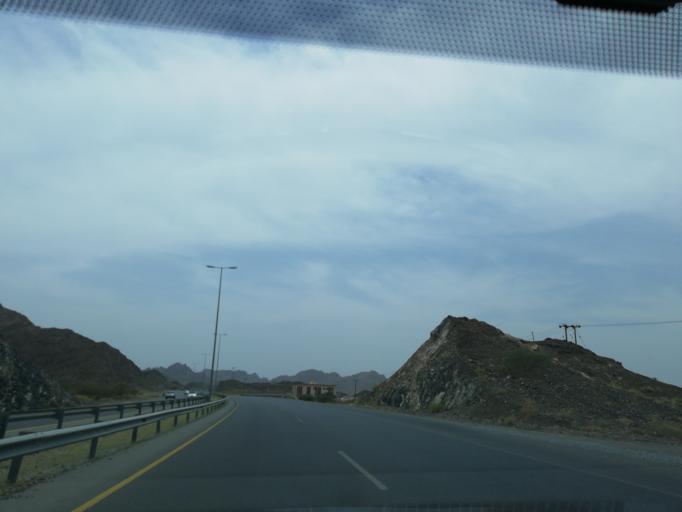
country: OM
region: Muhafazat ad Dakhiliyah
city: Izki
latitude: 22.9433
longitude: 57.7900
